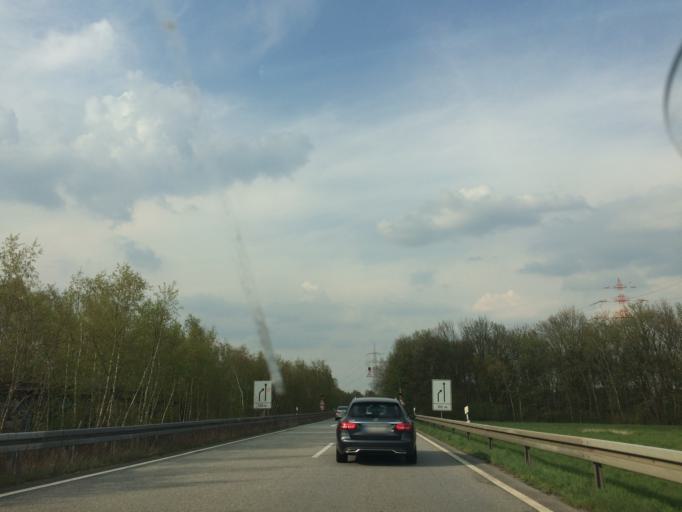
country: DE
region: North Rhine-Westphalia
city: Waltrop
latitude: 51.5838
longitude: 7.3672
